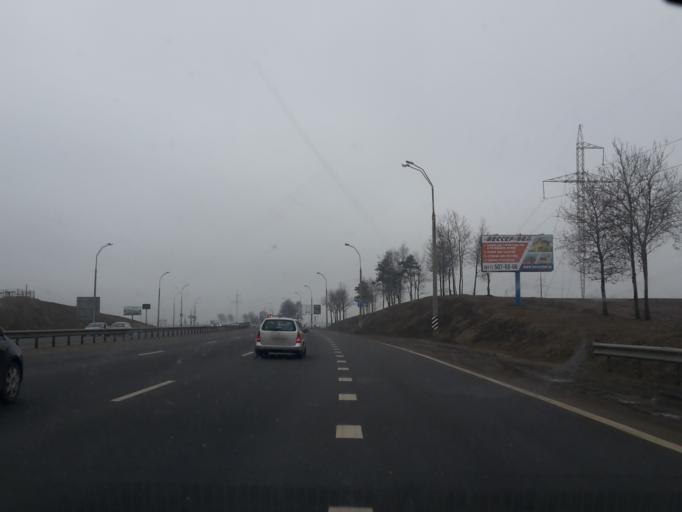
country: BY
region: Minsk
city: Zhdanovichy
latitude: 53.9074
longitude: 27.4078
